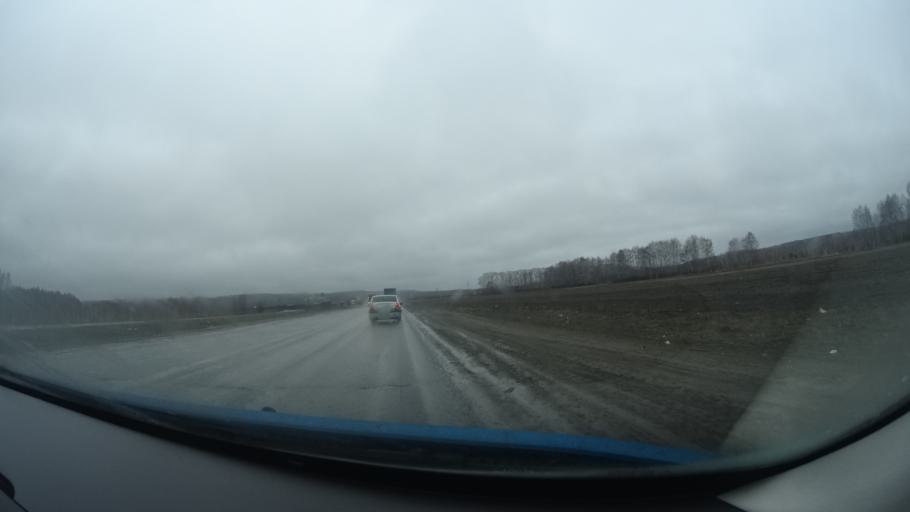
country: RU
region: Bashkortostan
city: Kandry
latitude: 54.6078
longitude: 54.3078
